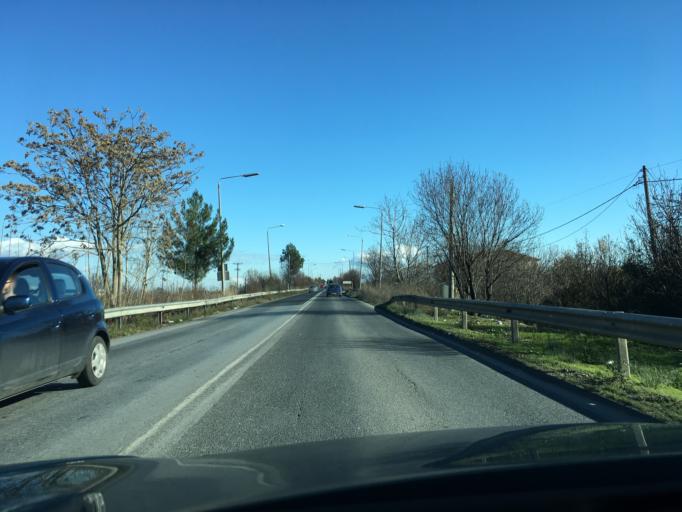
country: GR
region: Thessaly
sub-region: Nomos Larisis
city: Larisa
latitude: 39.6007
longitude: 22.4388
